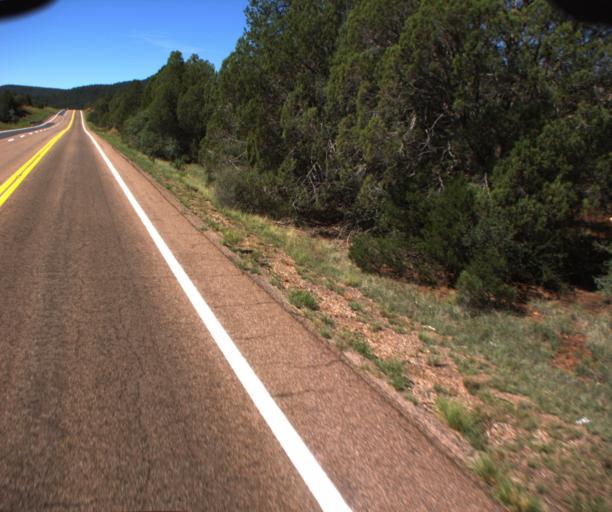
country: US
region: Arizona
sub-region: Navajo County
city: Cibecue
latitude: 33.9410
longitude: -110.3340
